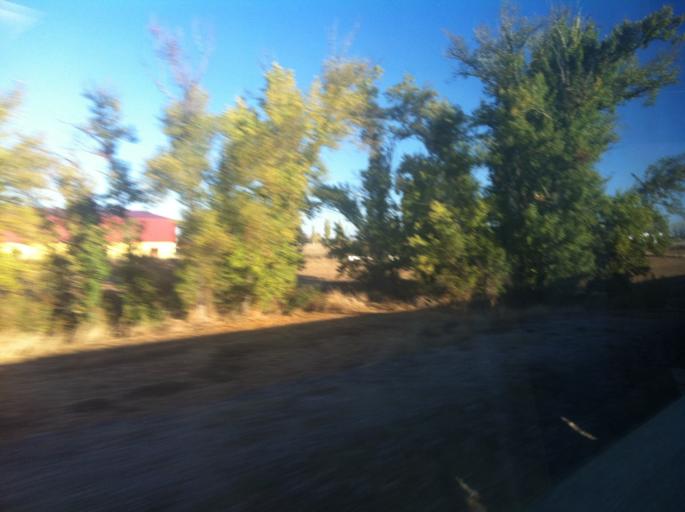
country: ES
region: Castille and Leon
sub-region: Provincia de Valladolid
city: Cabezon
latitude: 41.7490
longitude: -4.6400
